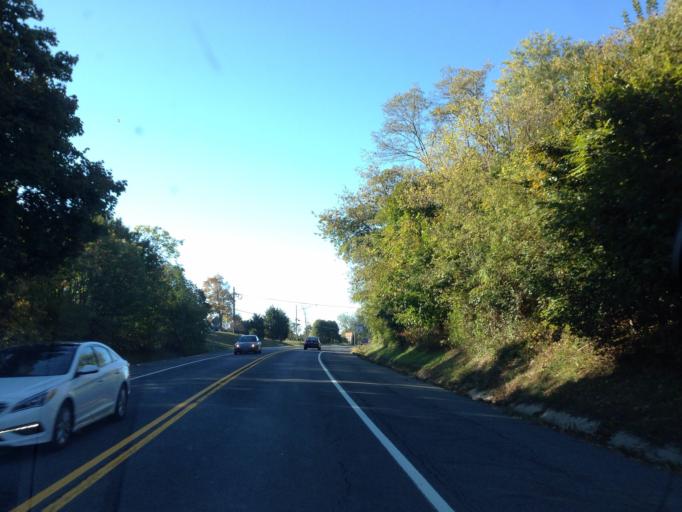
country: US
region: Maryland
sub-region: Montgomery County
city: Damascus
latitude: 39.2660
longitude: -77.2182
